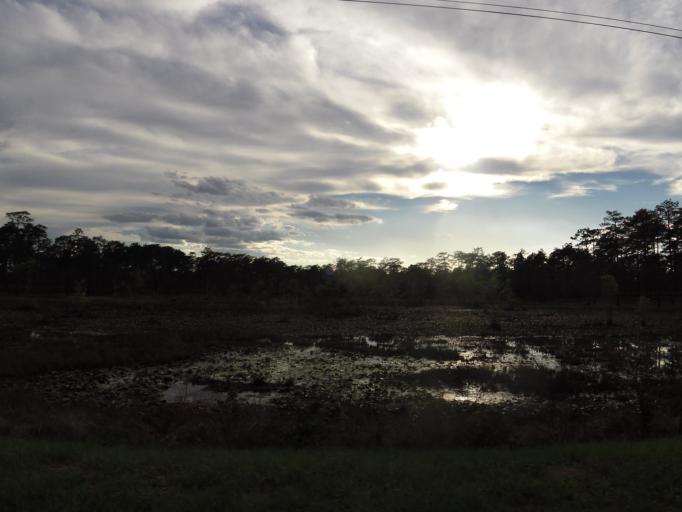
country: US
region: South Carolina
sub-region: Jasper County
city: Hardeeville
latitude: 32.3436
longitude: -81.0921
